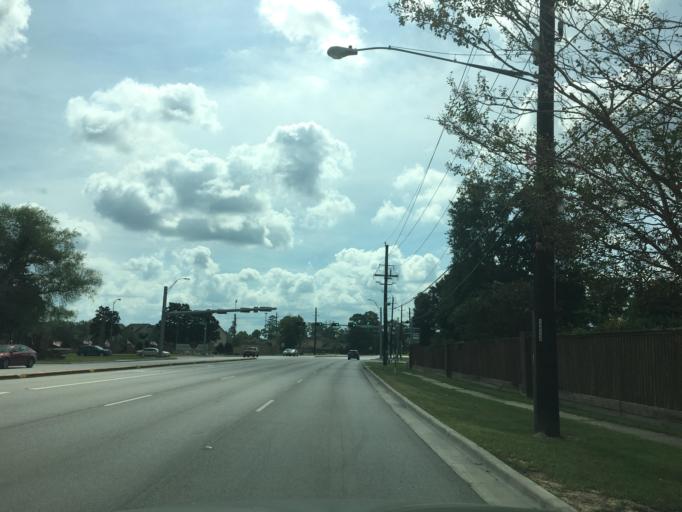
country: US
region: Texas
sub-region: Harris County
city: Spring
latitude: 30.1206
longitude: -95.3992
